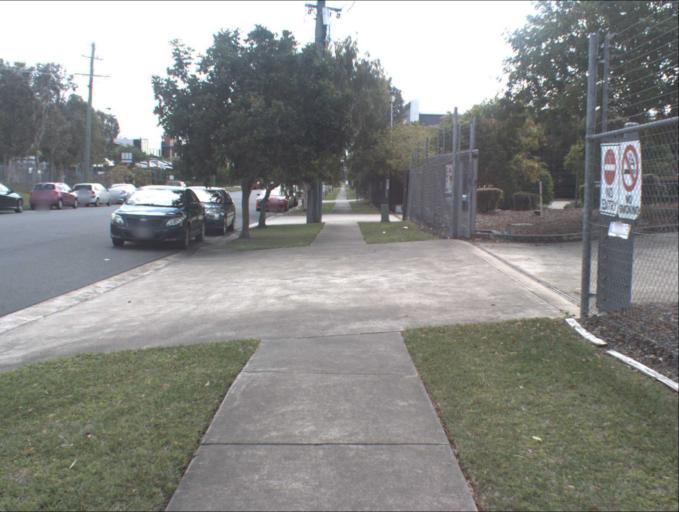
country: AU
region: Queensland
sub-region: Logan
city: Logan Reserve
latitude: -27.6865
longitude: 153.0755
